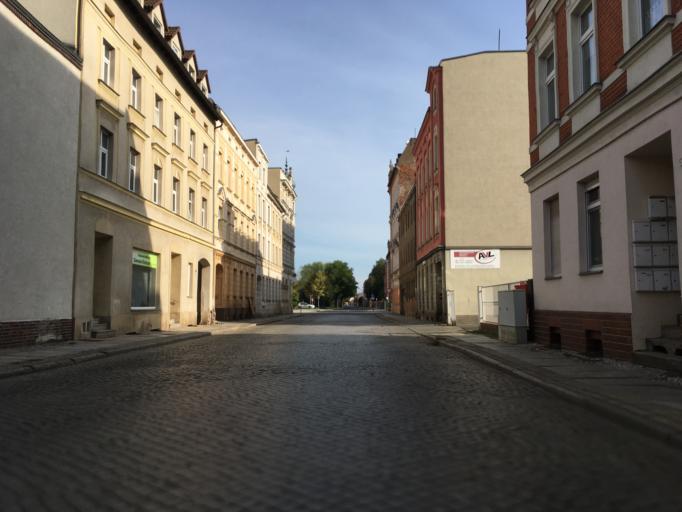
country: DE
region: Brandenburg
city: Forst
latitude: 51.7445
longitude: 14.6395
